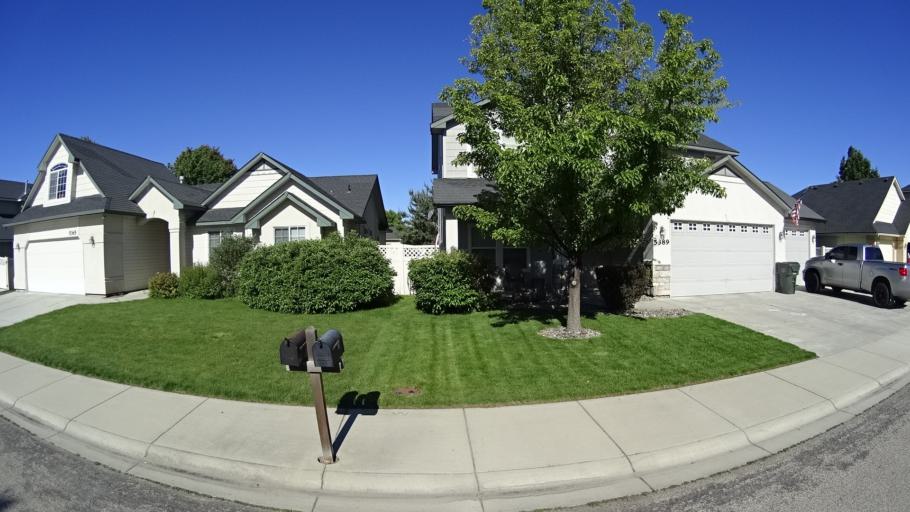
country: US
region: Idaho
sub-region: Ada County
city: Meridian
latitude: 43.6539
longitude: -116.4292
